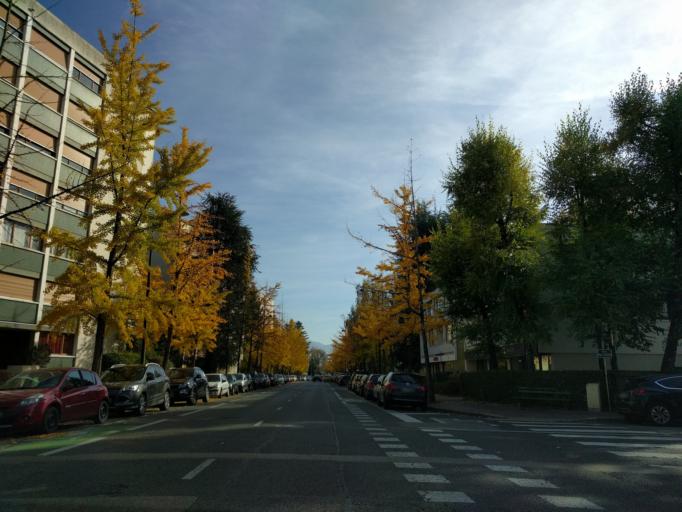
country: FR
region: Rhone-Alpes
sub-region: Departement de la Haute-Savoie
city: Annecy-le-Vieux
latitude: 45.9101
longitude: 6.1335
